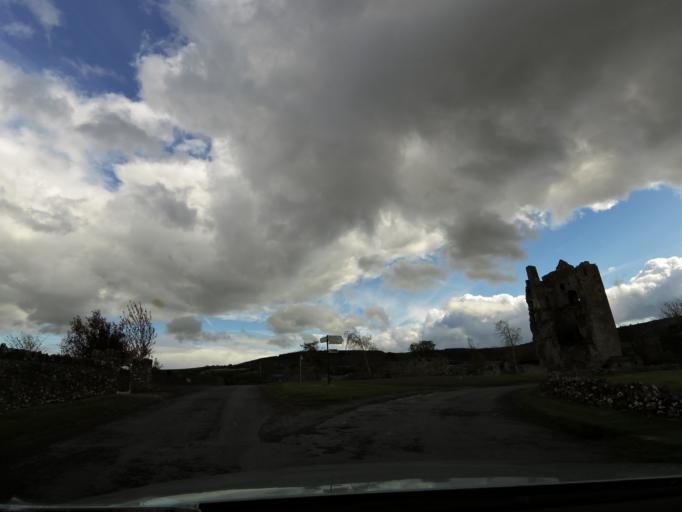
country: IE
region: Leinster
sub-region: Laois
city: Rathdowney
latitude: 52.8169
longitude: -7.4730
